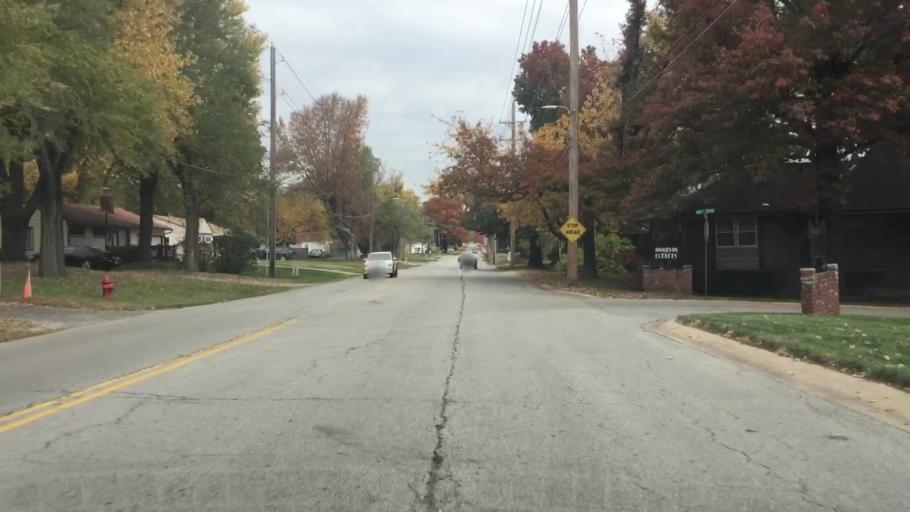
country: US
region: Missouri
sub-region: Jackson County
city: Raytown
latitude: 39.0125
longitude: -94.4447
